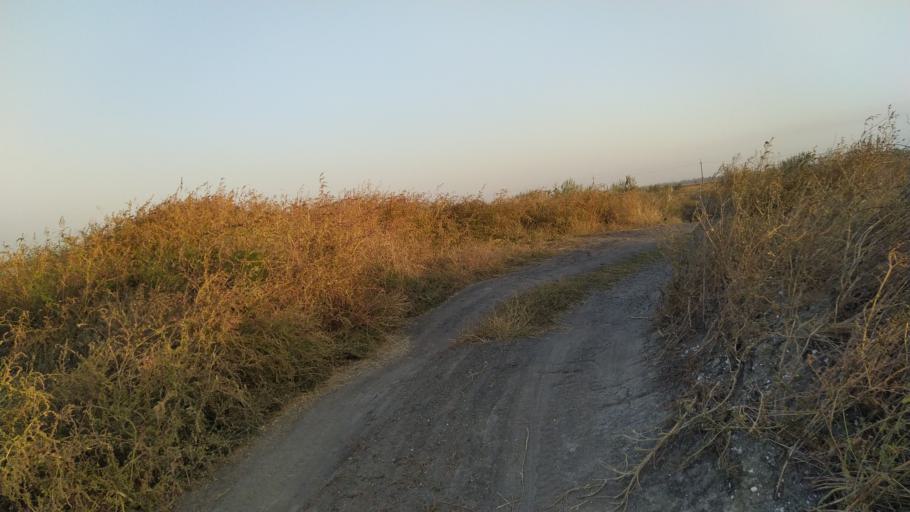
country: RU
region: Rostov
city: Kuleshovka
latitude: 47.1401
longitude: 39.6446
